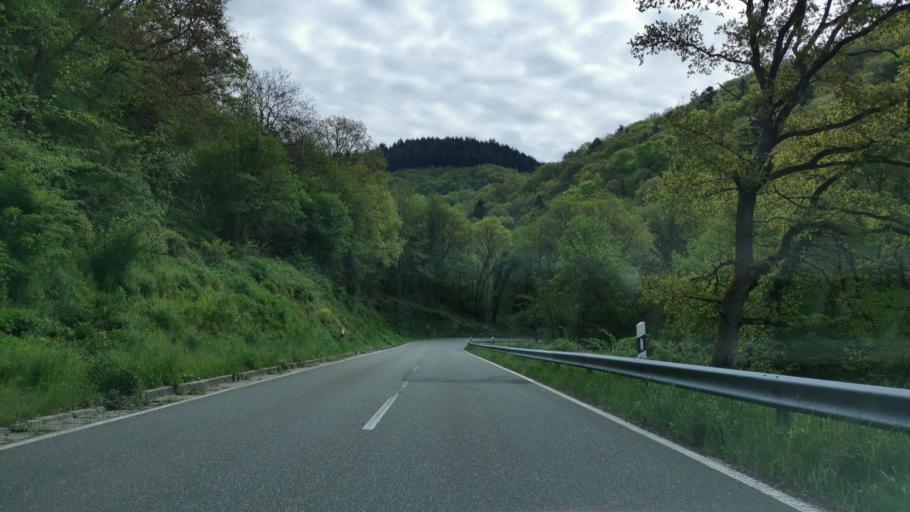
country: DE
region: Rheinland-Pfalz
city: Traben-Trarbach
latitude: 49.9403
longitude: 7.1260
